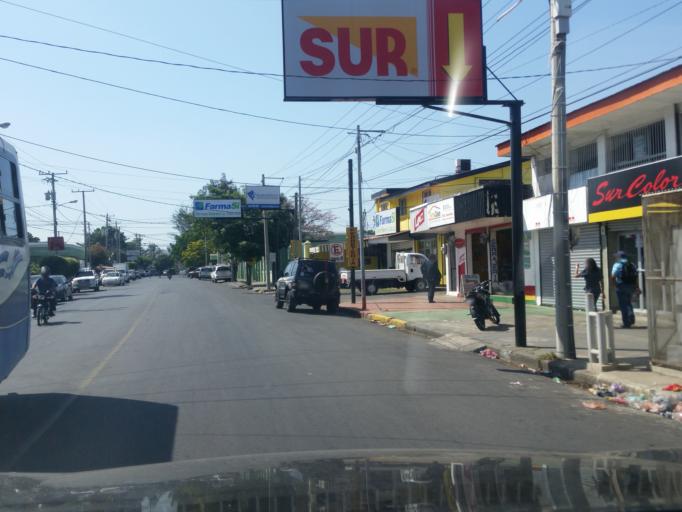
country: NI
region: Managua
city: Managua
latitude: 12.1479
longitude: -86.2879
